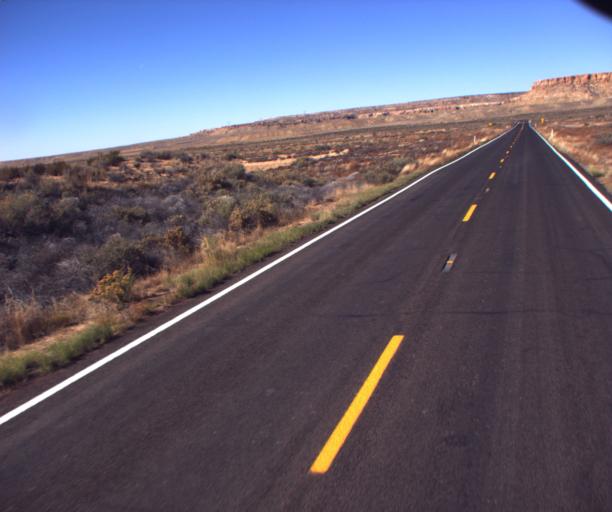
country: US
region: Arizona
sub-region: Navajo County
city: First Mesa
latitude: 35.9801
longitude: -110.7041
